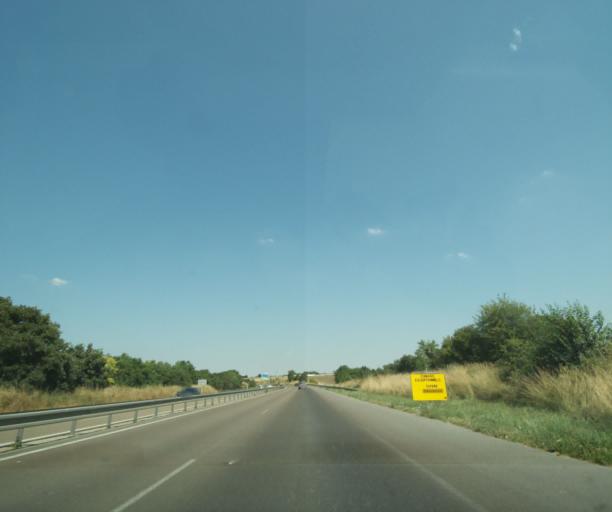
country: FR
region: Champagne-Ardenne
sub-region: Departement de la Marne
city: Saint-Memmie
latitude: 48.9709
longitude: 4.3814
